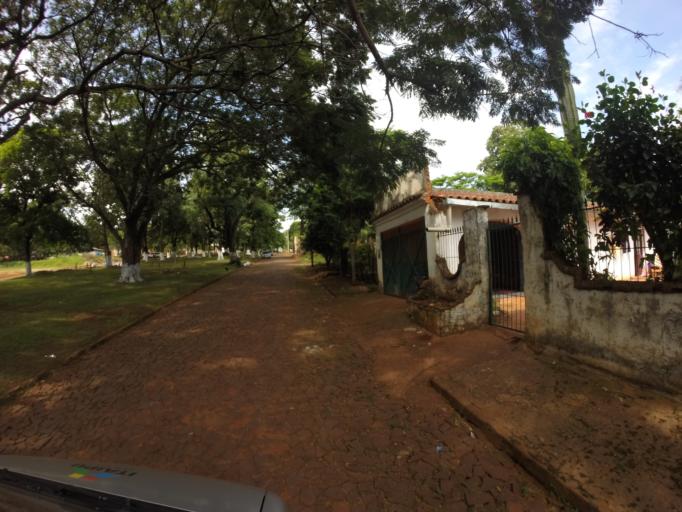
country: PY
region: Alto Parana
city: Ciudad del Este
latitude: -25.4399
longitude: -54.6438
